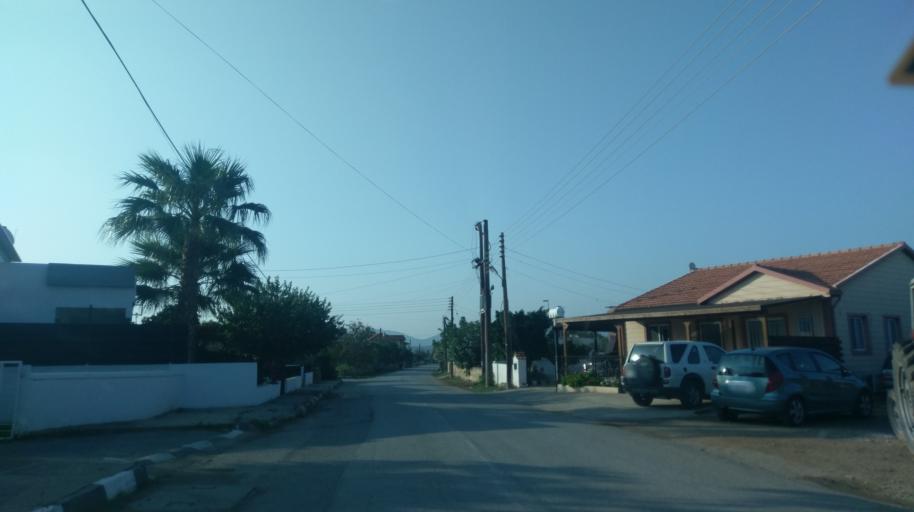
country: CY
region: Ammochostos
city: Leonarisso
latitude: 35.4245
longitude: 34.0688
